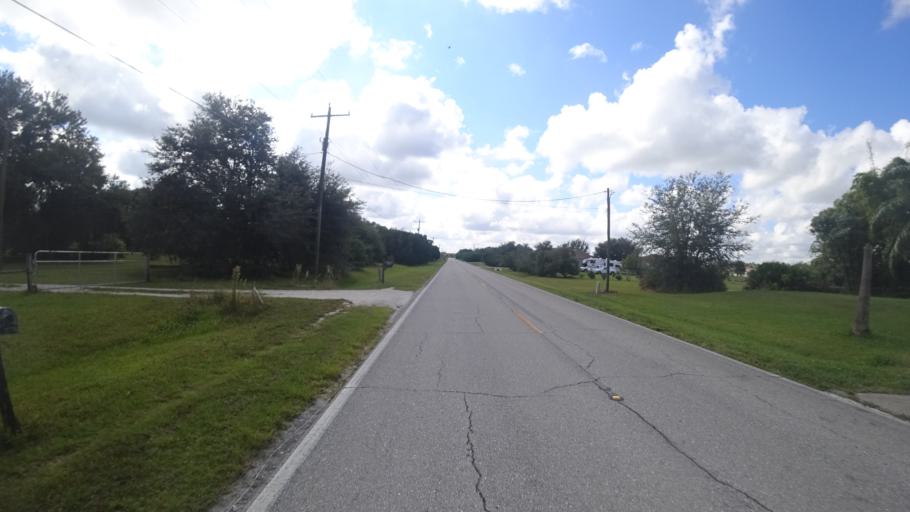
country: US
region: Florida
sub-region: Sarasota County
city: Lake Sarasota
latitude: 27.3933
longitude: -82.2711
